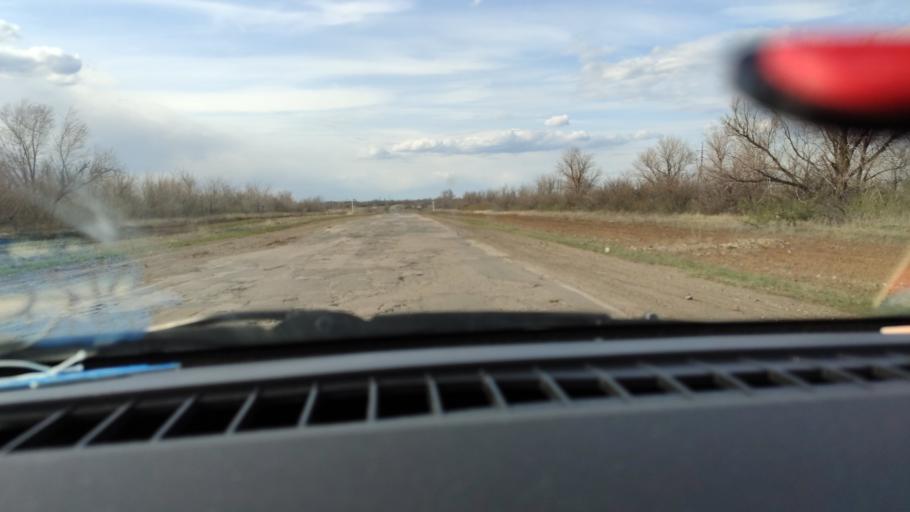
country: RU
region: Saratov
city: Rovnoye
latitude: 50.9585
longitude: 46.1198
